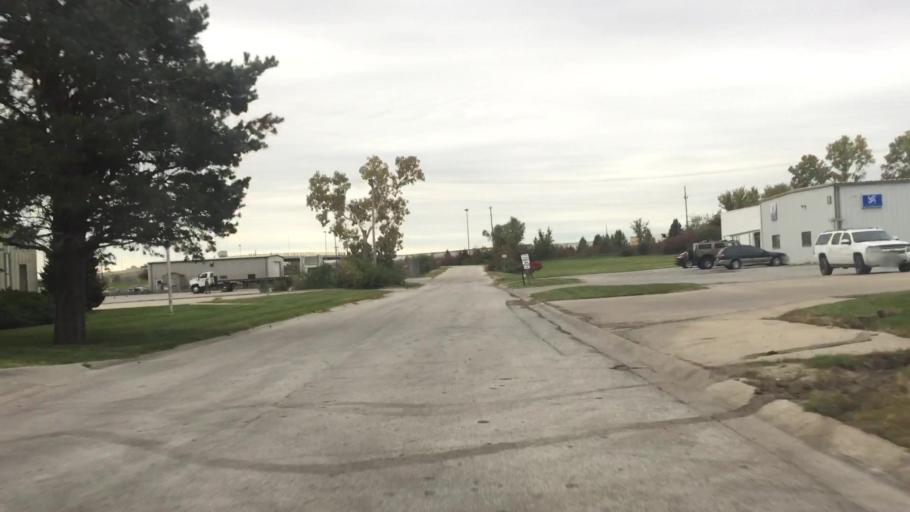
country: US
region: Missouri
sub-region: Jackson County
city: Lees Summit
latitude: 38.9008
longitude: -94.3689
